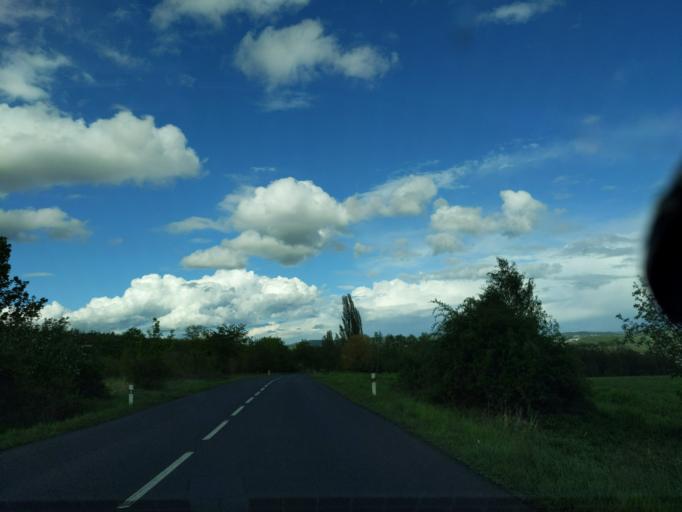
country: CZ
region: Ustecky
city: Chlumec
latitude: 50.6882
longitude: 13.9033
